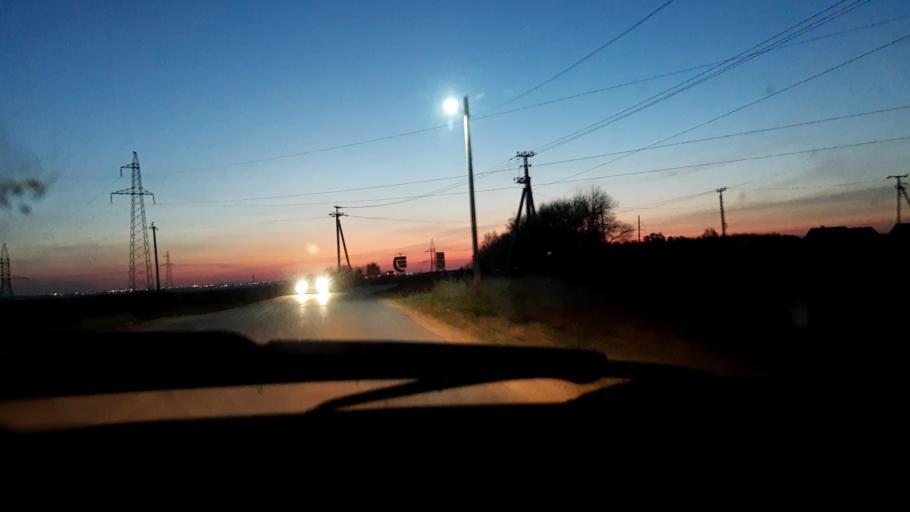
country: RU
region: Bashkortostan
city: Mikhaylovka
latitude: 54.8300
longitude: 55.8839
